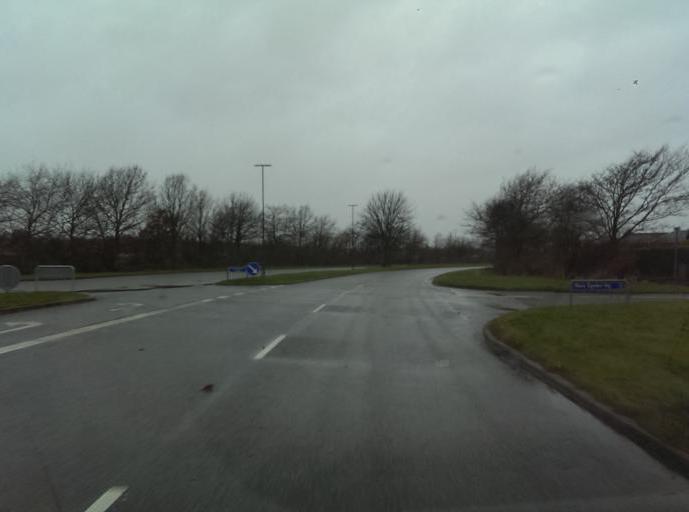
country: DK
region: South Denmark
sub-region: Esbjerg Kommune
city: Esbjerg
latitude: 55.5076
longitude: 8.4316
